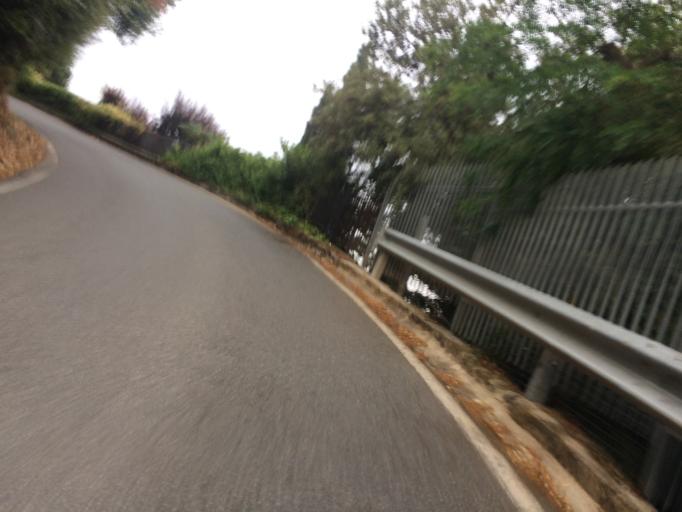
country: IT
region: Liguria
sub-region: Provincia di Imperia
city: San Remo
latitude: 43.8450
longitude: 7.7421
